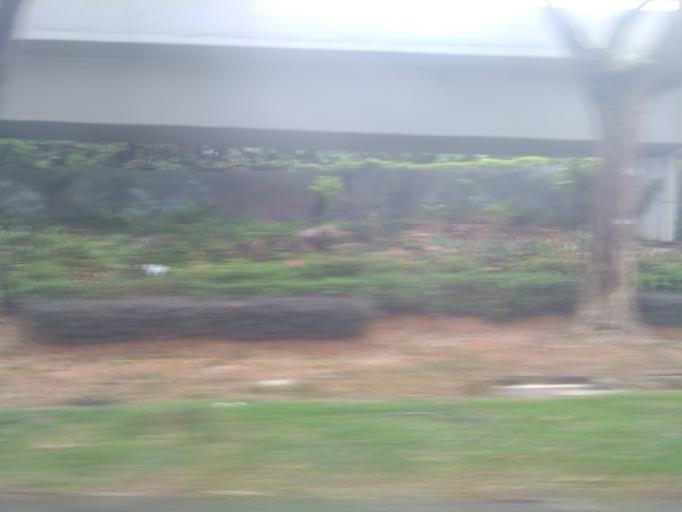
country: MY
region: Johor
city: Skudai
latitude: 1.5172
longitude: 103.6831
